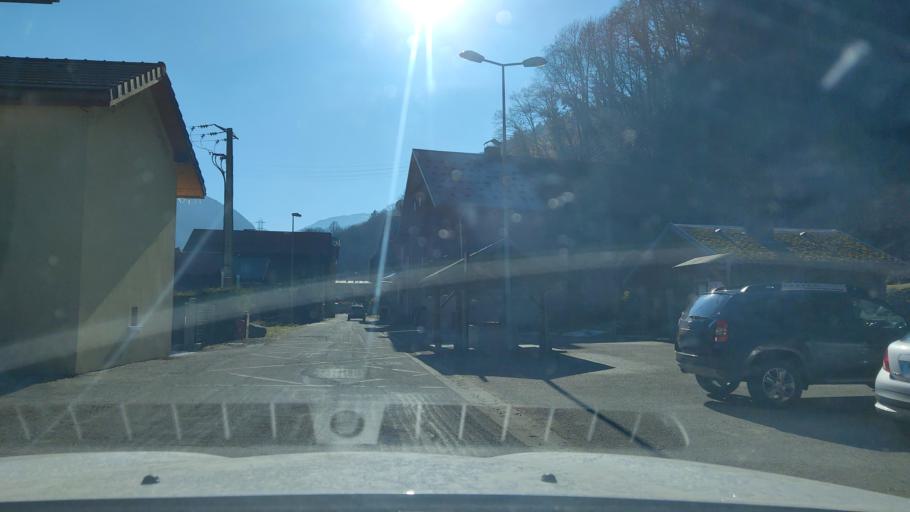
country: FR
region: Rhone-Alpes
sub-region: Departement de la Savoie
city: La Bathie
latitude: 45.5649
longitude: 6.4635
